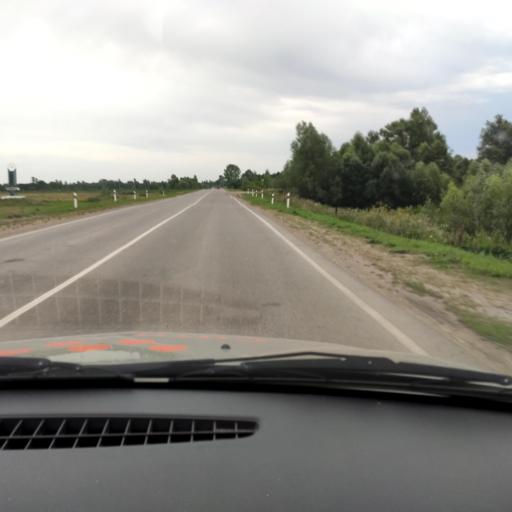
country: RU
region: Bashkortostan
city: Krasnaya Gorka
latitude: 55.1752
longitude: 56.6669
